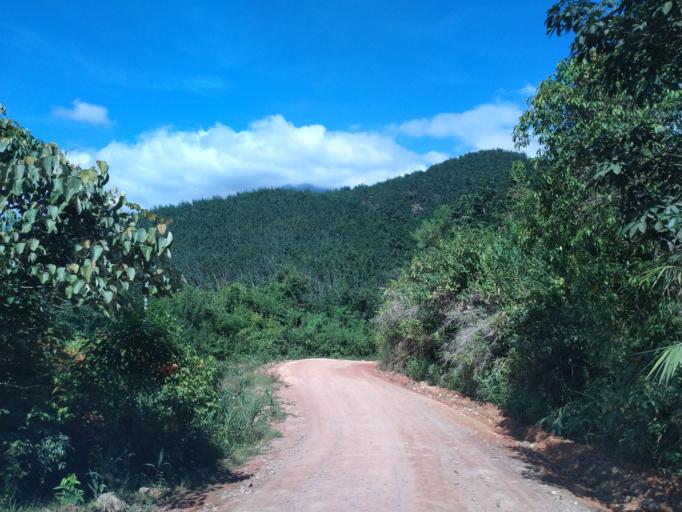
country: TH
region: Changwat Bueng Kan
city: Pak Khat
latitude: 18.6349
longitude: 103.0112
